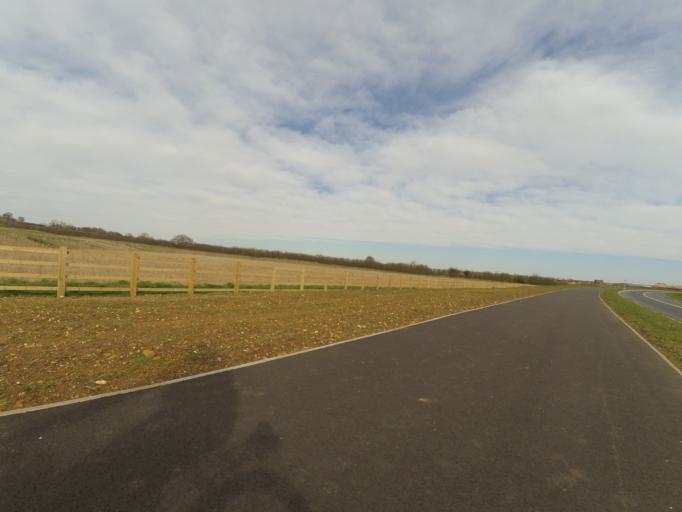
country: GB
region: England
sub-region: Warwickshire
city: Rugby
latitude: 52.3697
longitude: -1.2131
